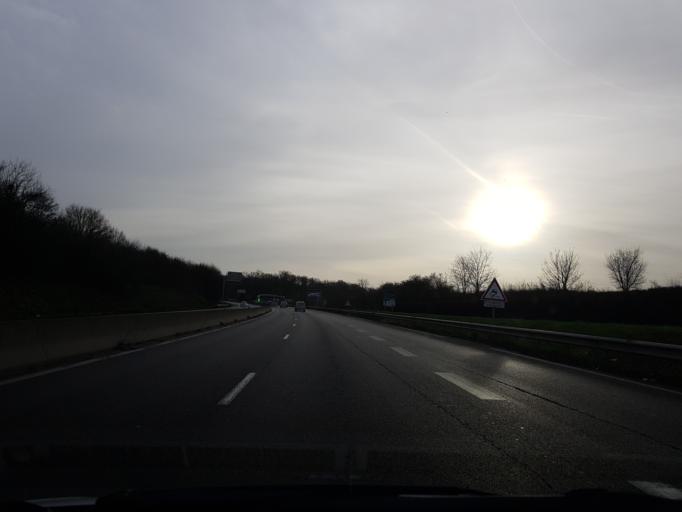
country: FR
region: Ile-de-France
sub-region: Departement de l'Essonne
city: Montgeron
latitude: 48.6922
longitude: 2.4504
